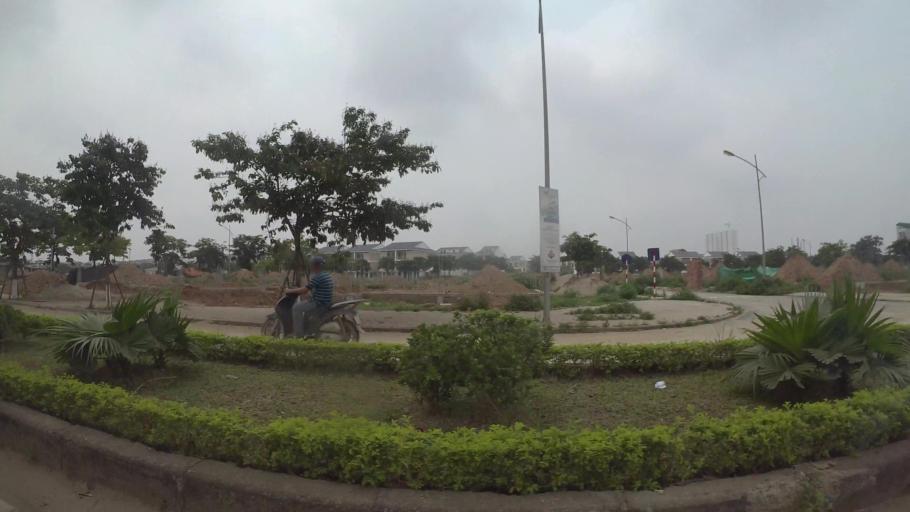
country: VN
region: Ha Noi
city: Ha Dong
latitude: 20.9844
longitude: 105.7532
